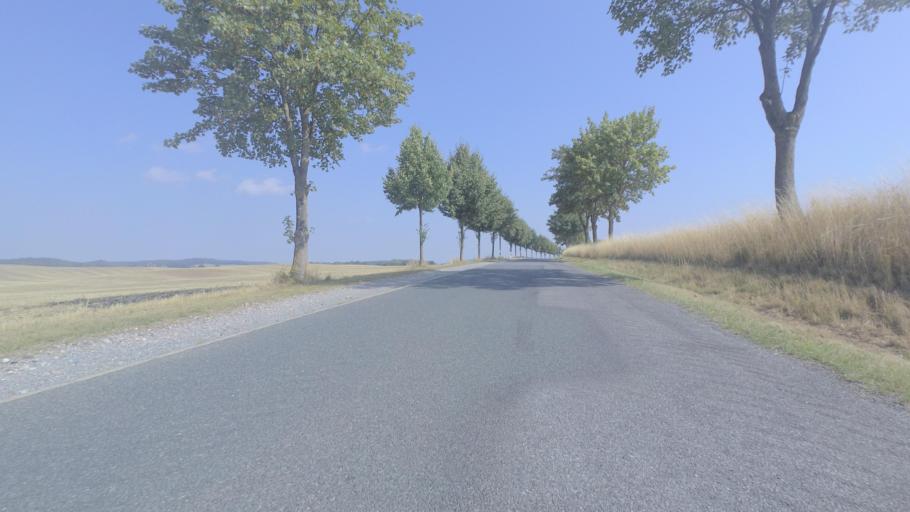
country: DE
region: Mecklenburg-Vorpommern
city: Pampow
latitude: 53.6946
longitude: 12.5993
